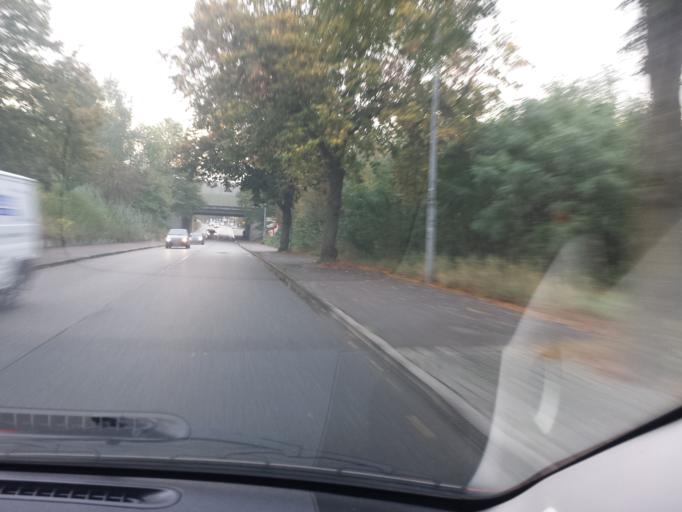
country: DE
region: Bavaria
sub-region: Upper Bavaria
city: Lenting
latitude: 48.7687
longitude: 11.4587
